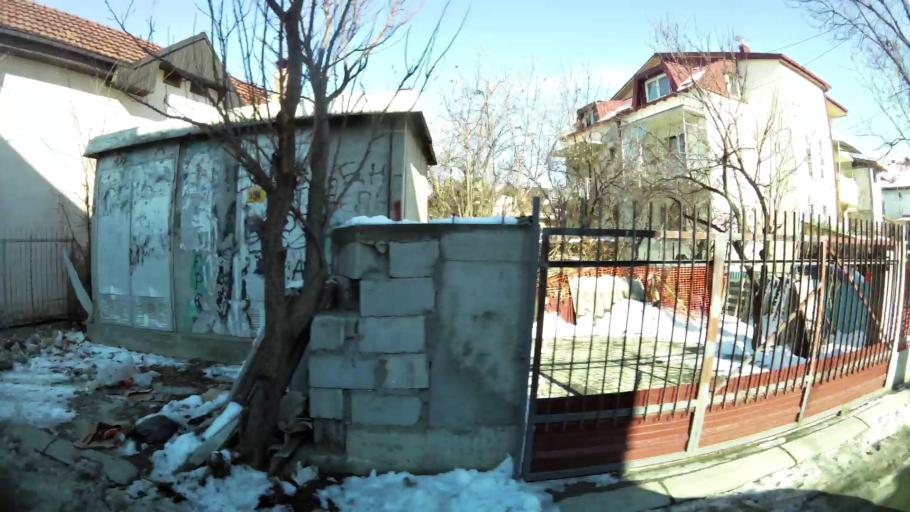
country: MK
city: Krushopek
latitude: 42.0025
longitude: 21.3541
